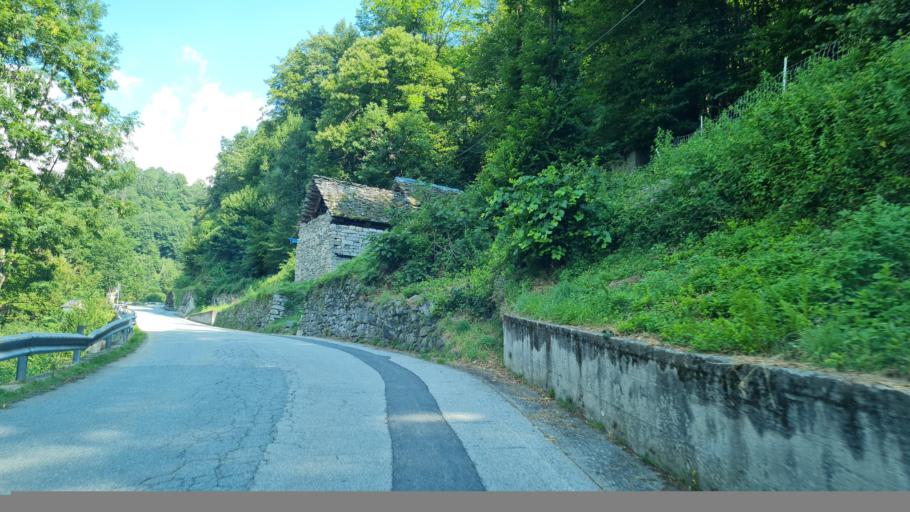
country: IT
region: Piedmont
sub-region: Provincia Verbano-Cusio-Ossola
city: Baceno
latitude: 46.2662
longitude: 8.3164
